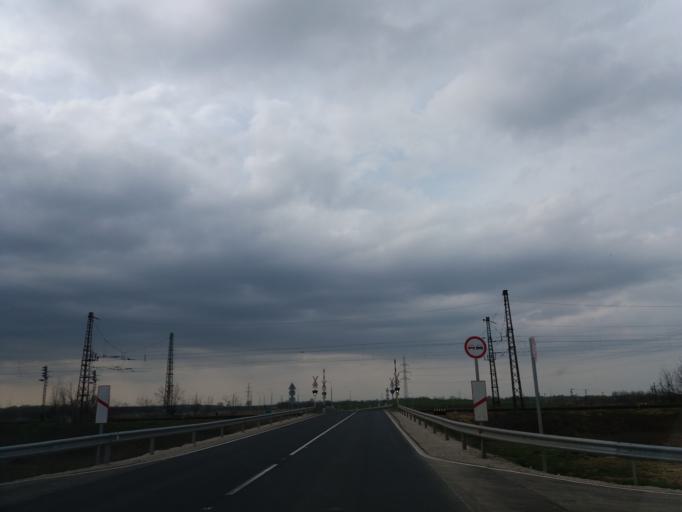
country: HU
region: Szabolcs-Szatmar-Bereg
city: Kisvarda
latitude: 48.2015
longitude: 22.0709
